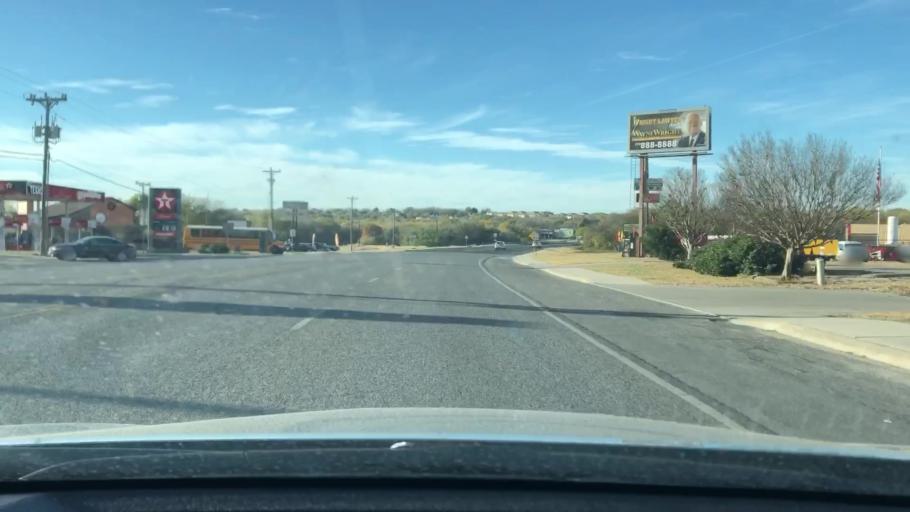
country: US
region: Texas
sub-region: Bexar County
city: Converse
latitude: 29.5078
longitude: -98.3089
